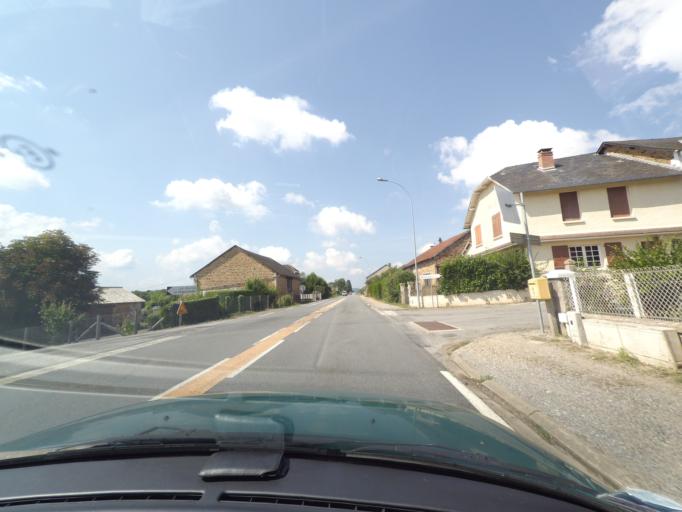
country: FR
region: Limousin
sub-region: Departement de la Haute-Vienne
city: Neuvic-Entier
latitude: 45.7310
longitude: 1.6657
